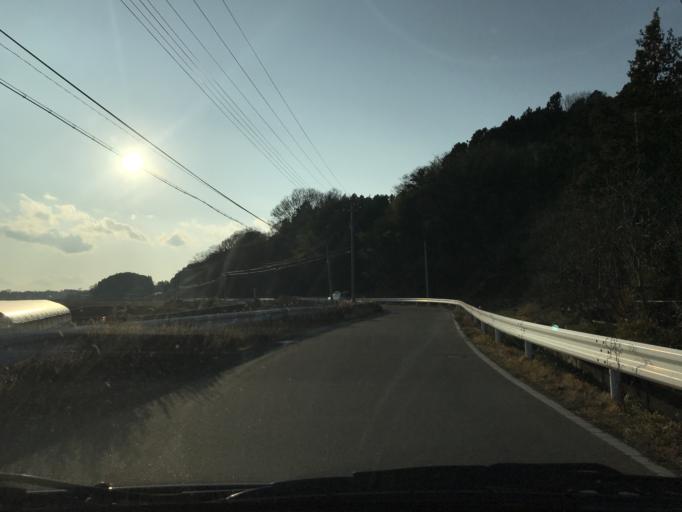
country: JP
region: Miyagi
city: Wakuya
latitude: 38.7173
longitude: 141.1377
